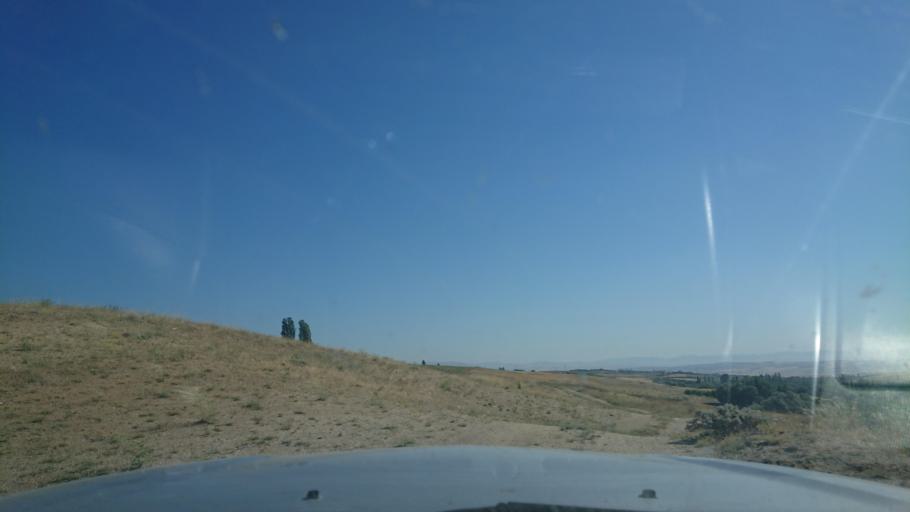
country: TR
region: Aksaray
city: Agacoren
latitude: 38.8469
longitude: 33.9266
